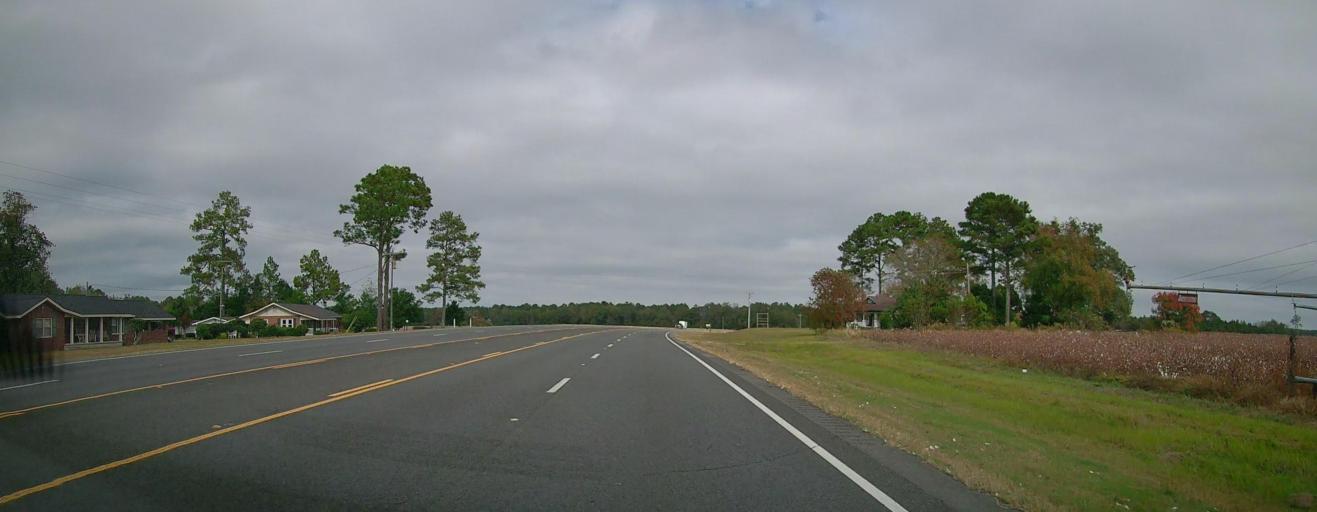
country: US
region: Georgia
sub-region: Colquitt County
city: Moultrie
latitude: 31.0771
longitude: -83.8208
